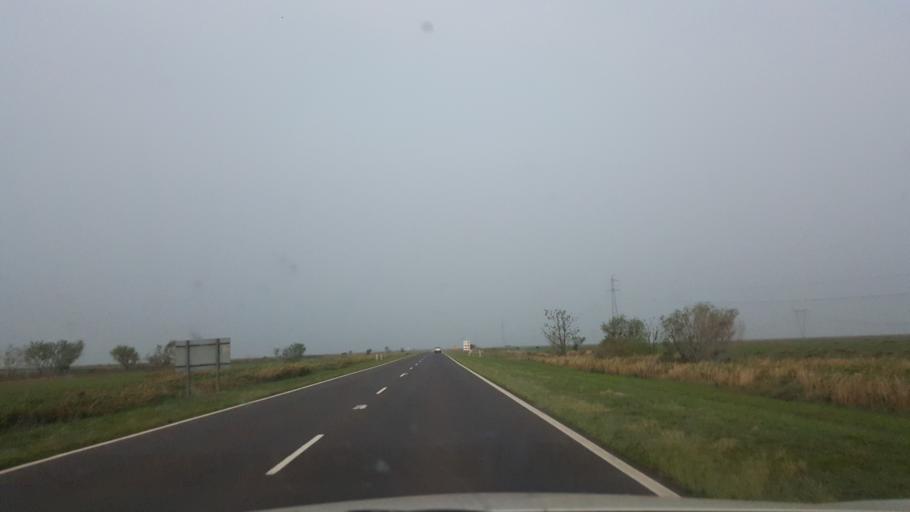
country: AR
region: Corrientes
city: Ita Ibate
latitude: -27.5556
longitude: -57.1457
